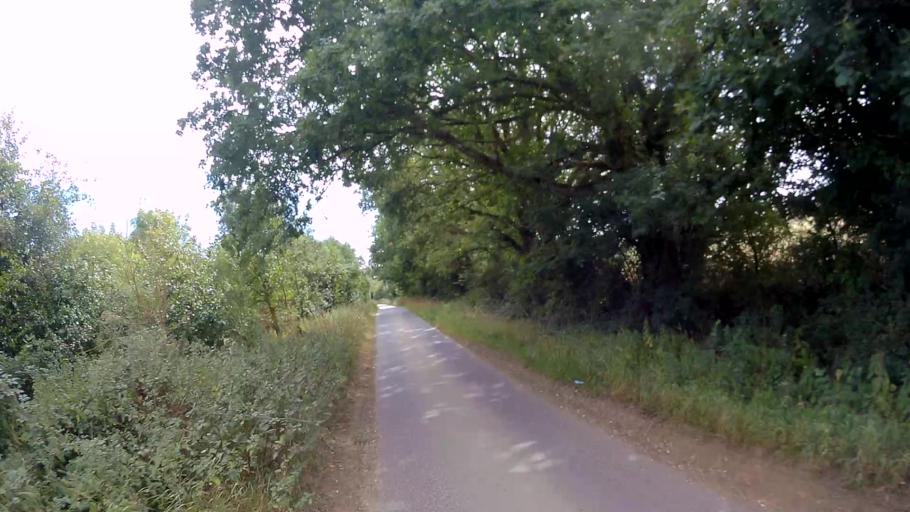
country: GB
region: England
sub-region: Hampshire
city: Odiham
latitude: 51.2320
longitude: -0.9623
